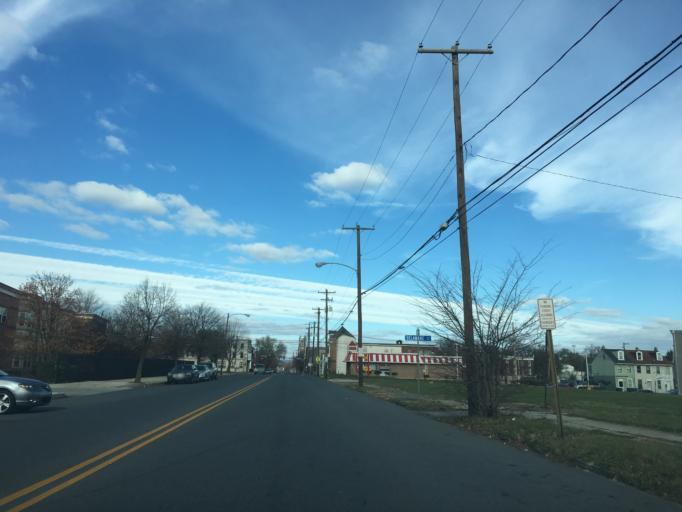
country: US
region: Pennsylvania
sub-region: Dauphin County
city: Harrisburg
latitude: 40.2788
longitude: -76.8895
